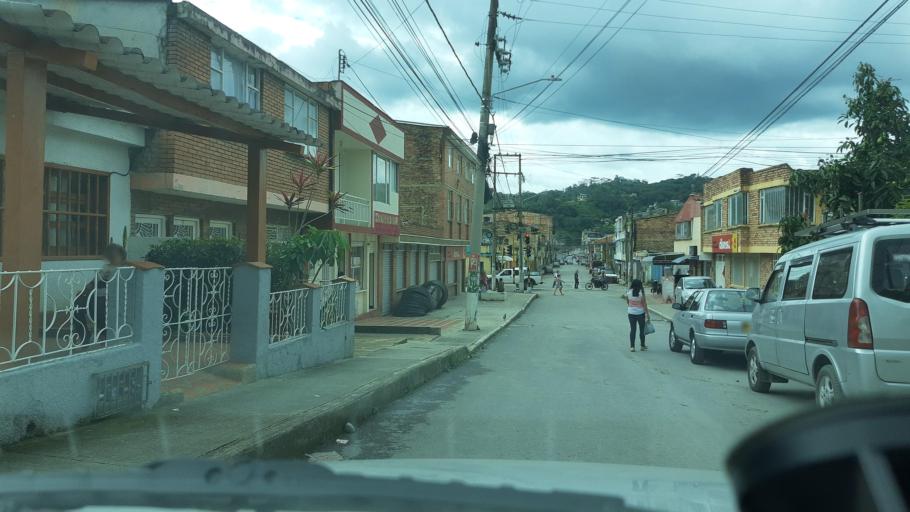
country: CO
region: Boyaca
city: Moniquira
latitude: 5.8769
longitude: -73.5745
